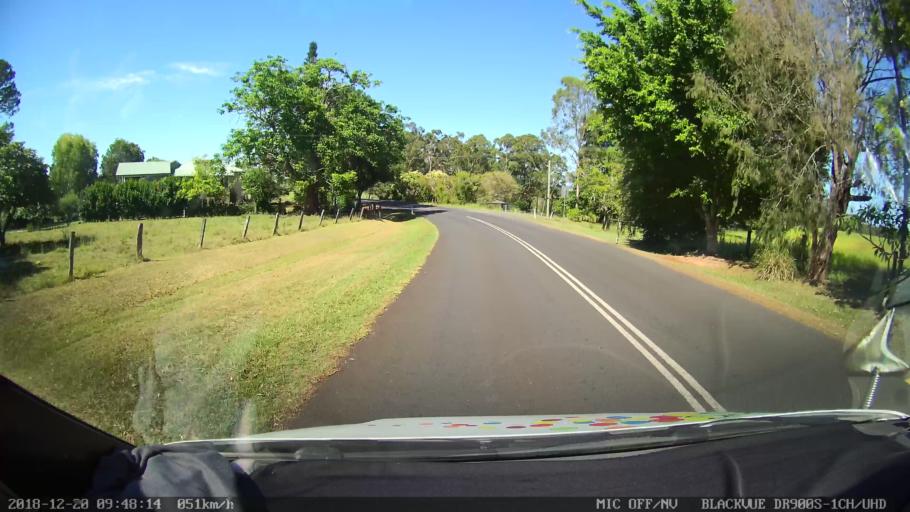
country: AU
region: New South Wales
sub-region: Lismore Municipality
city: Lismore
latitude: -28.7685
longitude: 153.2927
